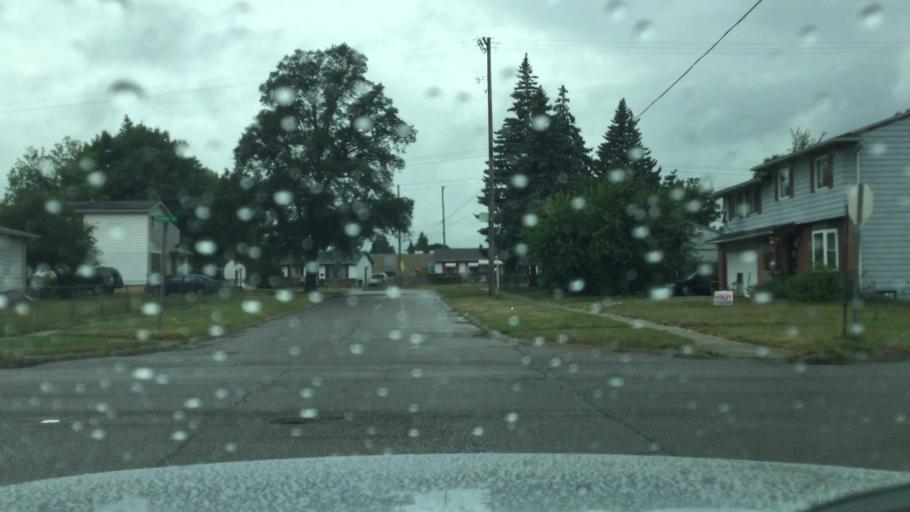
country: US
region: Michigan
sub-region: Genesee County
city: Beecher
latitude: 43.0707
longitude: -83.7234
